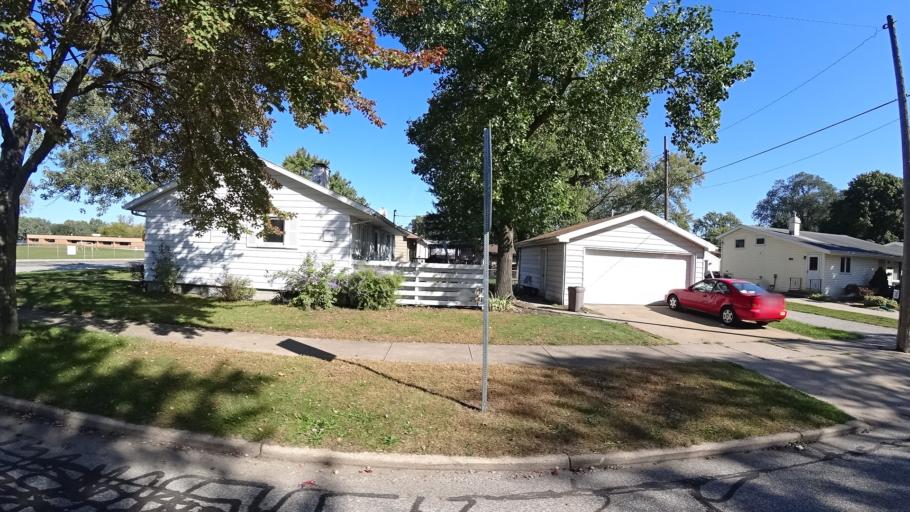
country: US
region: Indiana
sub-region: LaPorte County
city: Michigan City
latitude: 41.6946
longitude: -86.9083
